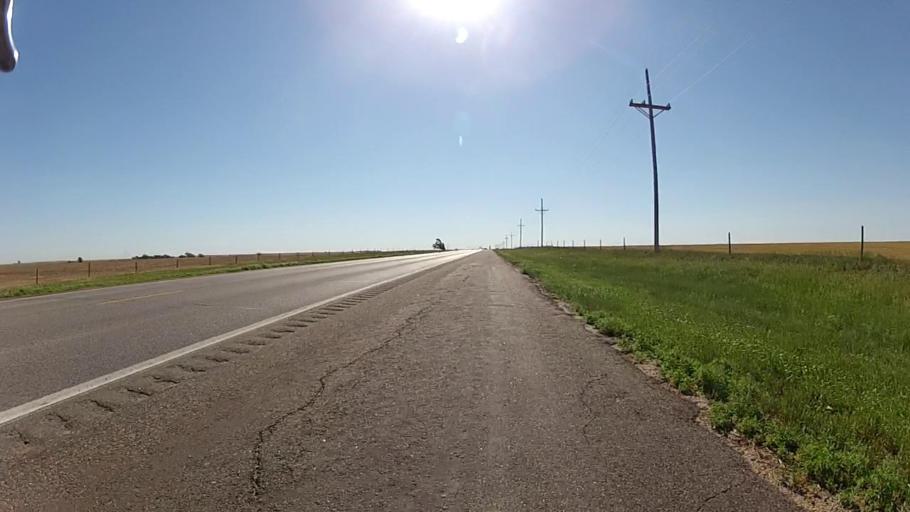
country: US
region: Kansas
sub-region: Ford County
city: Dodge City
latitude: 37.5863
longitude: -99.6759
